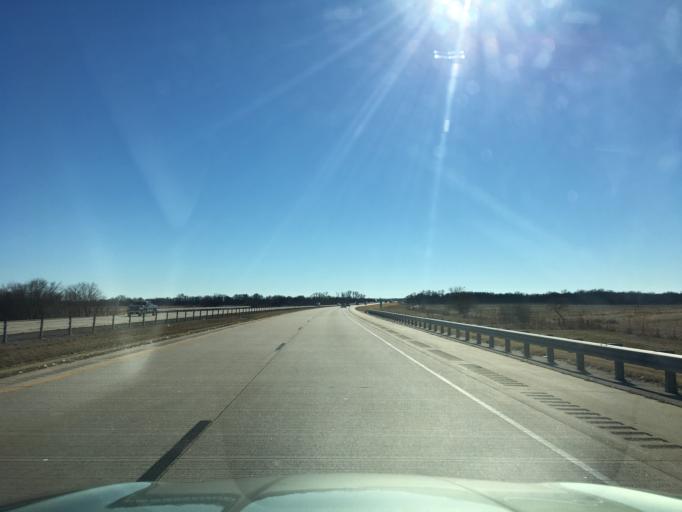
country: US
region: Oklahoma
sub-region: Kay County
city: Tonkawa
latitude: 36.4856
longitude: -97.3279
